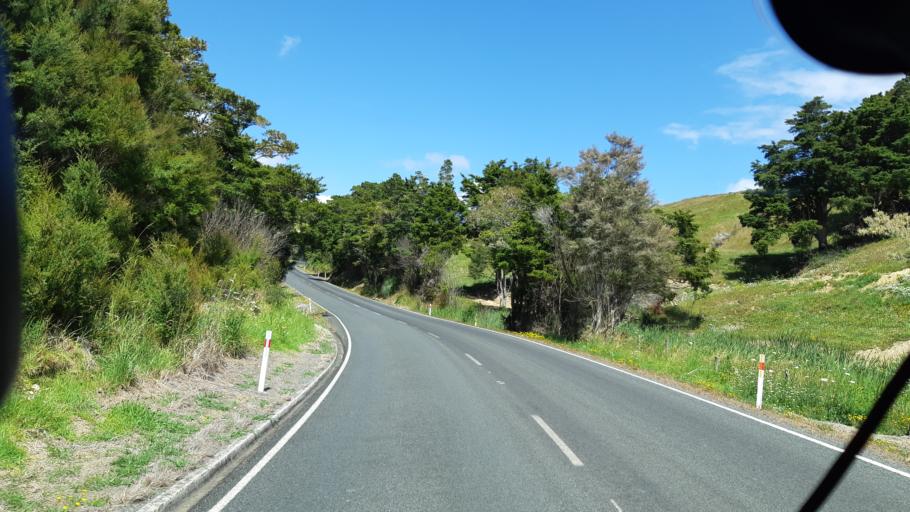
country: NZ
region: Northland
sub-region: Far North District
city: Kaitaia
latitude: -35.2701
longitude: 173.4867
